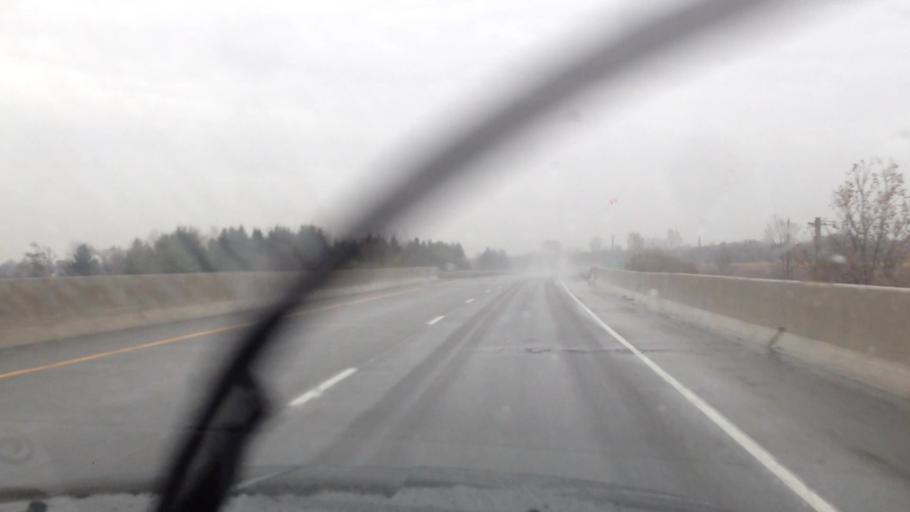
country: CA
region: Ontario
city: Casselman
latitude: 45.3040
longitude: -75.1034
